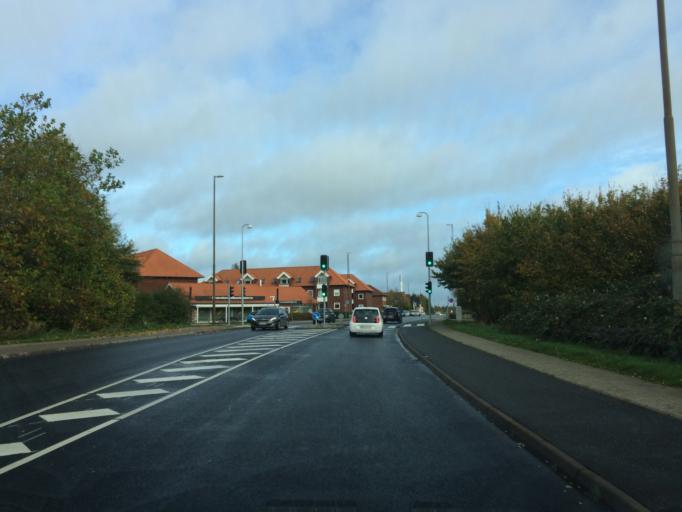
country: DK
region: South Denmark
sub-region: Fredericia Kommune
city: Fredericia
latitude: 55.5738
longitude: 9.7433
